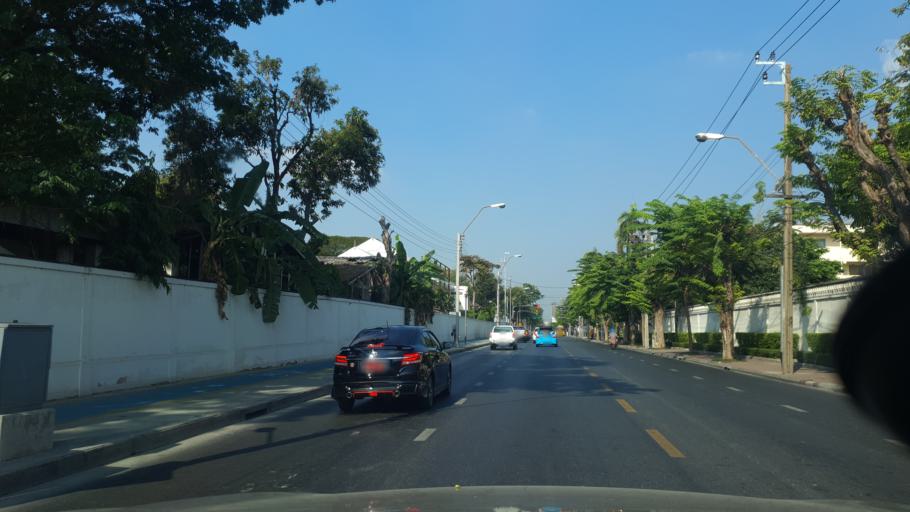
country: TH
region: Bangkok
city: Dusit
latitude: 13.7746
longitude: 100.5167
